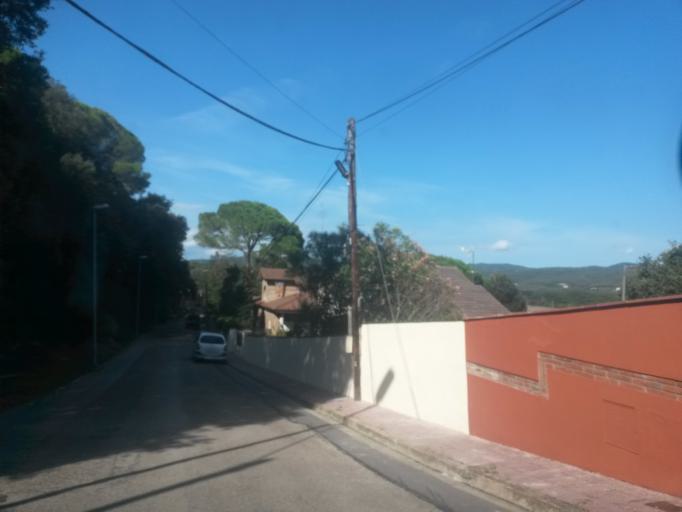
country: ES
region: Catalonia
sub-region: Provincia de Girona
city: Fornells de la Selva
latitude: 41.9479
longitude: 2.8184
